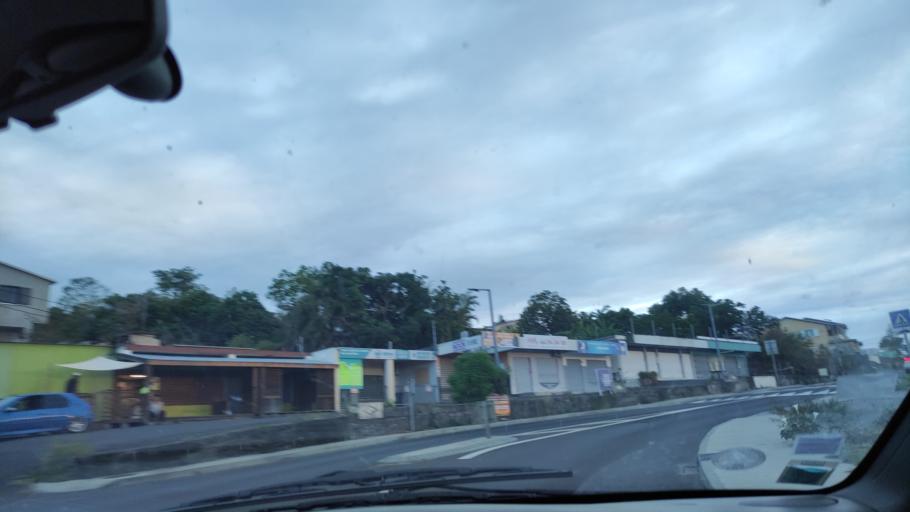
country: RE
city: Piton Saint-Leu
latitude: -21.2072
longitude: 55.2971
